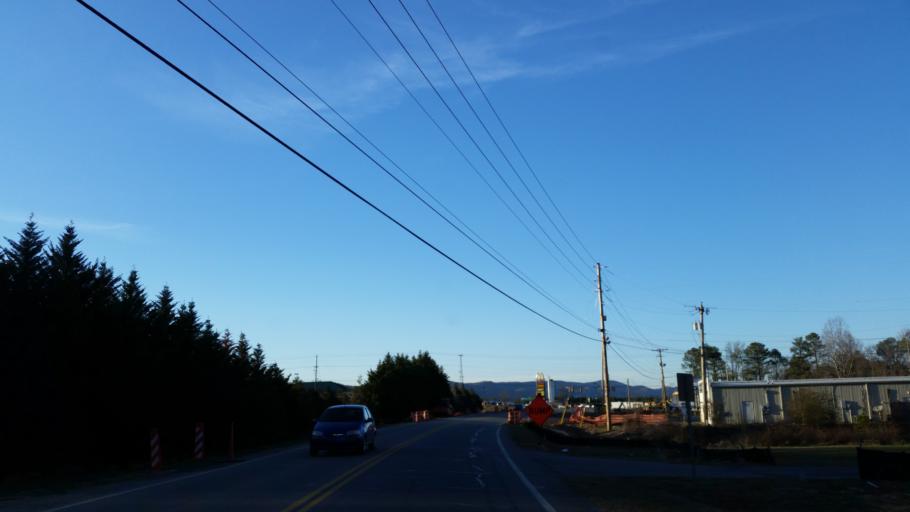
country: US
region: Georgia
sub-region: Whitfield County
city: Dalton
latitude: 34.6533
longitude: -84.9775
